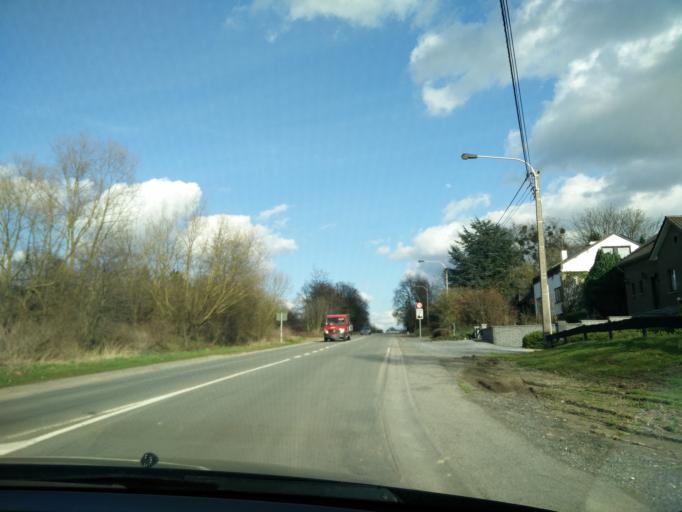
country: BE
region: Wallonia
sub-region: Province de Liege
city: Dalhem
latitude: 50.7404
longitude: 5.7310
